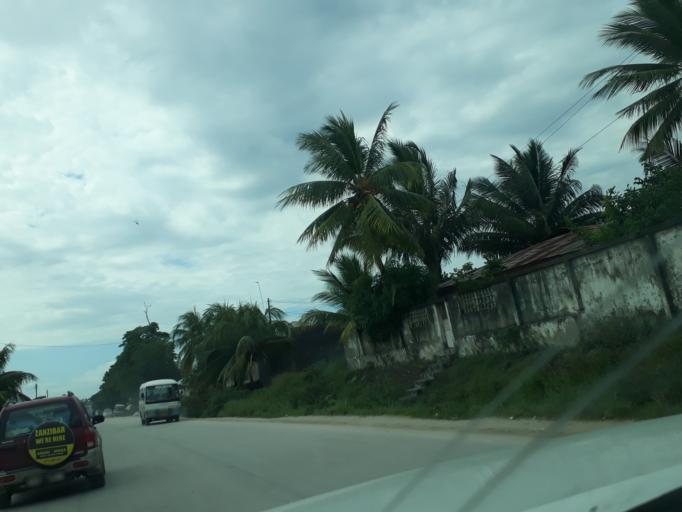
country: TZ
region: Zanzibar Central/South
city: Koani
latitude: -6.0876
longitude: 39.2226
